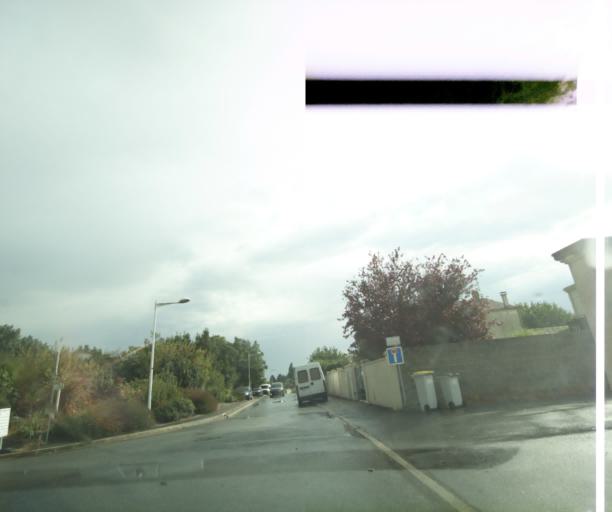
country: FR
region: Poitou-Charentes
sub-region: Departement de la Charente-Maritime
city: Tonnay-Charente
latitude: 45.9503
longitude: -0.8822
